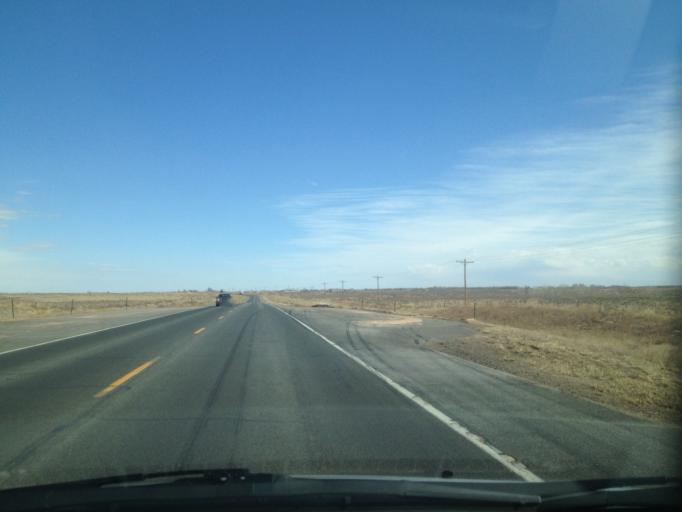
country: US
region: Colorado
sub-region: Weld County
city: Kersey
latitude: 40.2923
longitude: -104.2802
